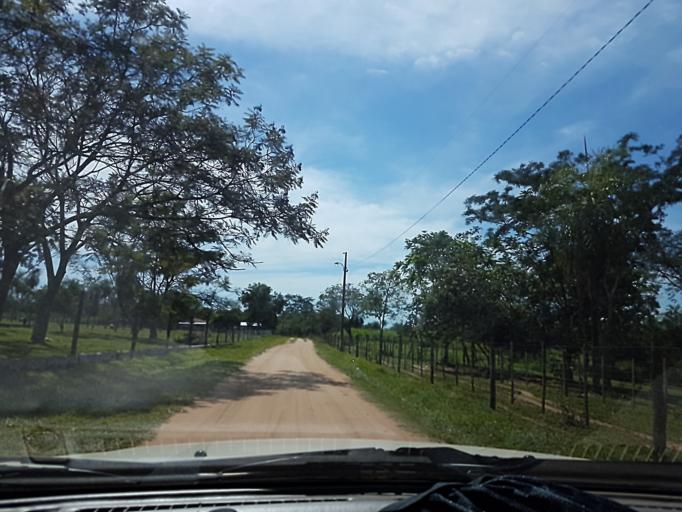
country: PY
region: Cordillera
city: Arroyos y Esteros
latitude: -24.9855
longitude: -57.1998
